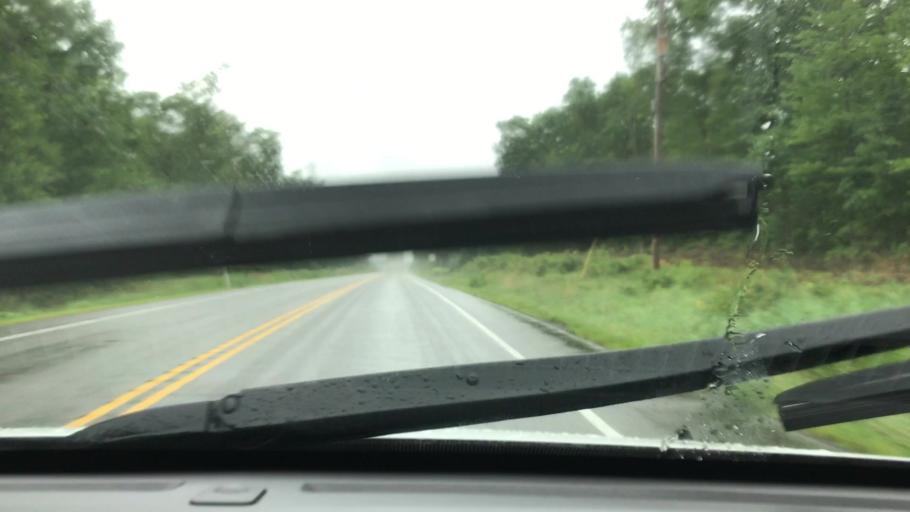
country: US
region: Pennsylvania
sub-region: Clearfield County
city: Osceola Mills
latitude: 40.8116
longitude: -78.2250
